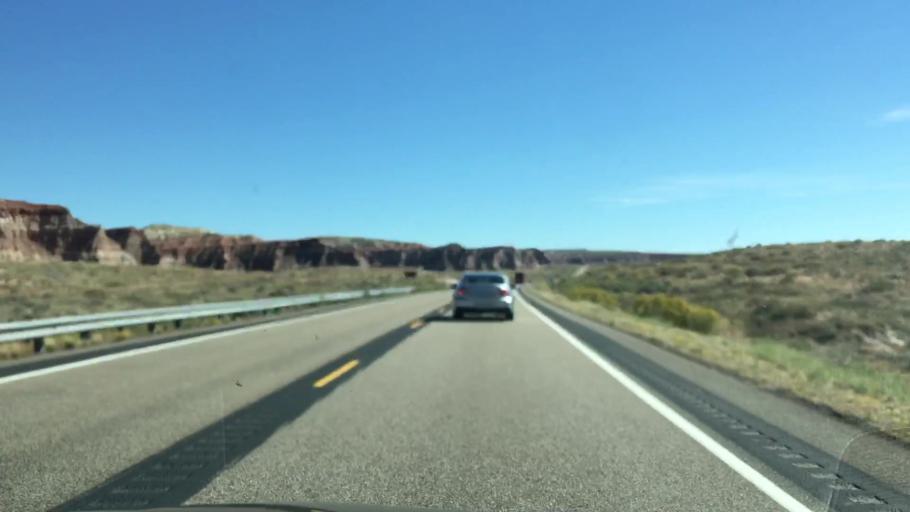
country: US
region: Arizona
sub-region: Coconino County
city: Page
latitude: 37.1061
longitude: -111.8943
